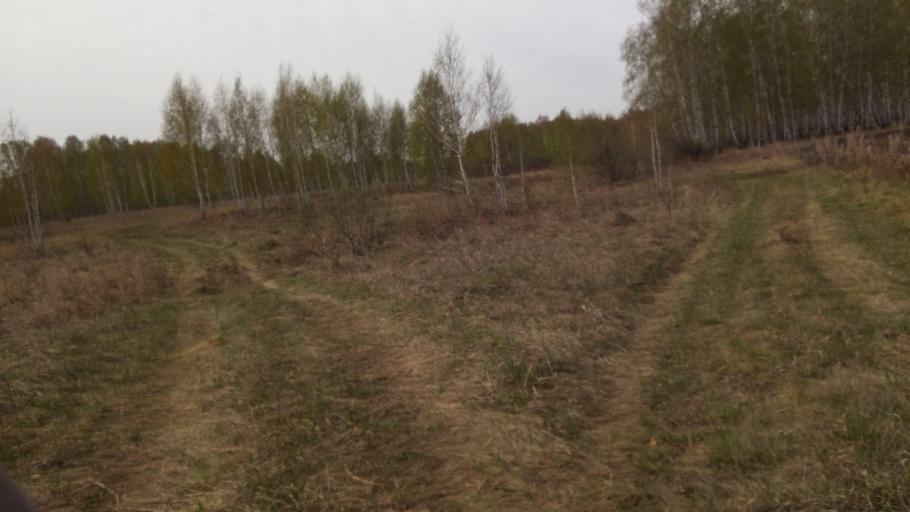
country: RU
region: Chelyabinsk
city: Timiryazevskiy
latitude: 55.0053
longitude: 60.8546
